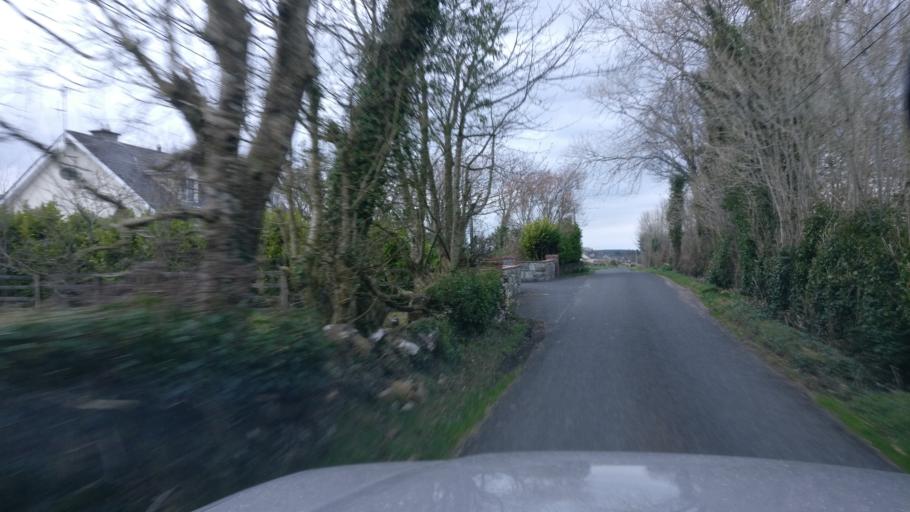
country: IE
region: Connaught
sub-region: County Galway
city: Loughrea
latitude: 53.2536
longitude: -8.5109
